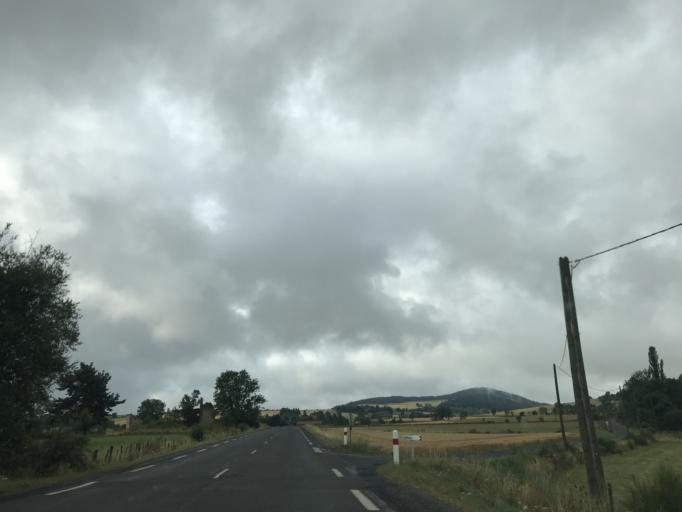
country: FR
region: Auvergne
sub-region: Departement de la Haute-Loire
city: Saint-Paulien
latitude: 45.1967
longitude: 3.8213
